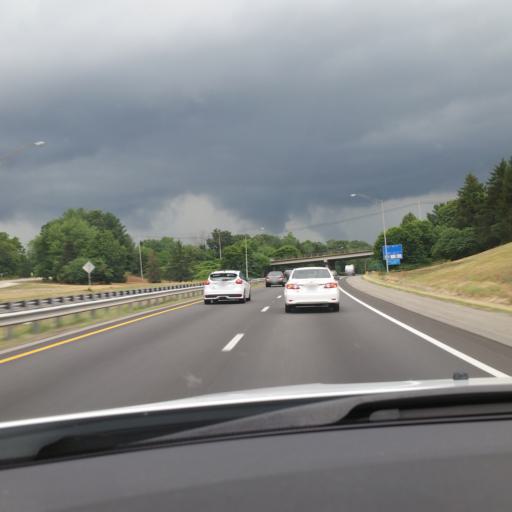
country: US
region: North Carolina
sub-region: Buncombe County
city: Woodfin
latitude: 35.6290
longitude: -82.5801
